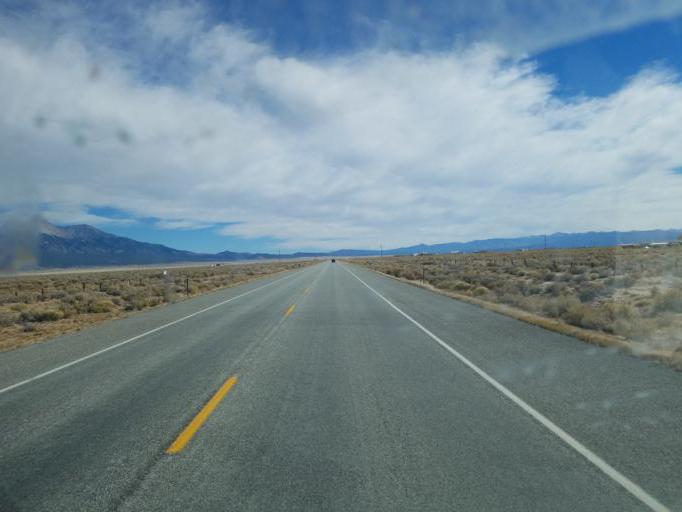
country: US
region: Colorado
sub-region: Alamosa County
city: Alamosa East
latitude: 37.4749
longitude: -105.7039
